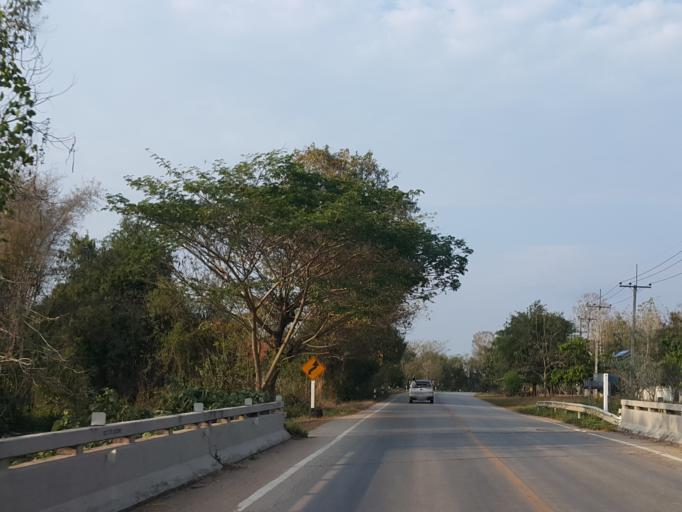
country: TH
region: Lampang
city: Chae Hom
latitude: 18.5224
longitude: 99.4768
